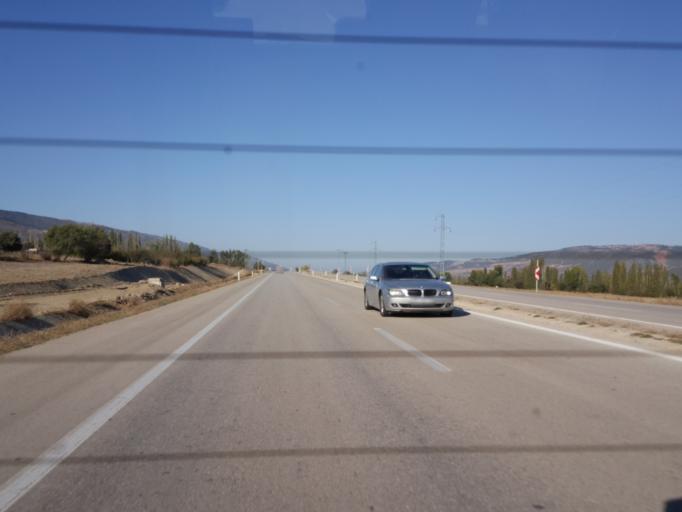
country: TR
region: Amasya
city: Ezinepazari
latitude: 40.5693
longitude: 36.0830
